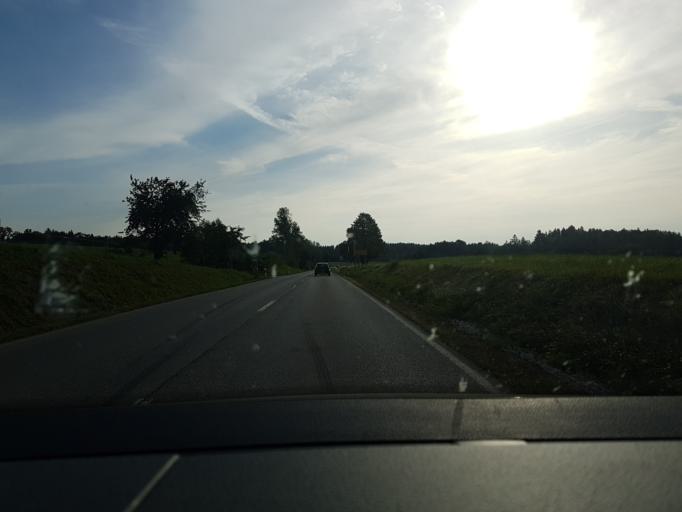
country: DE
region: Bavaria
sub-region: Upper Bavaria
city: Teisendorf
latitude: 47.8432
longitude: 12.8521
